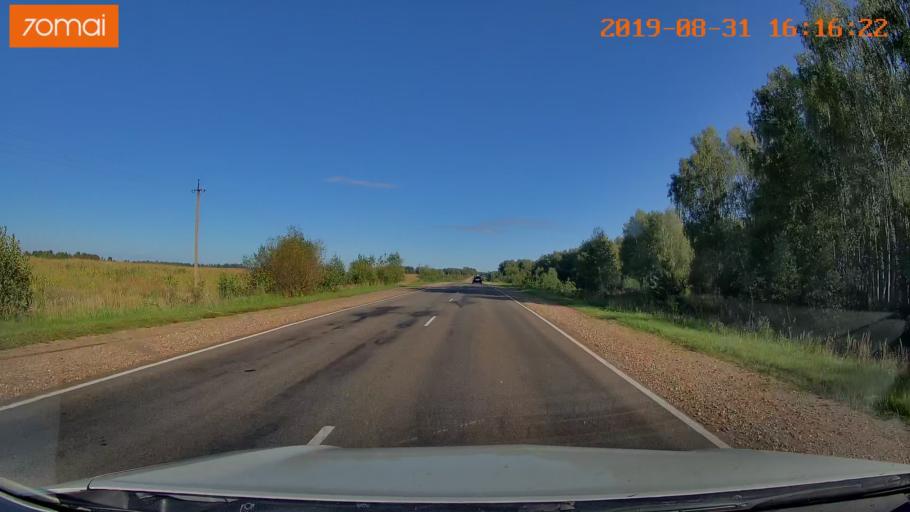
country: RU
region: Kaluga
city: Nikola-Lenivets
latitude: 54.5534
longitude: 35.5094
